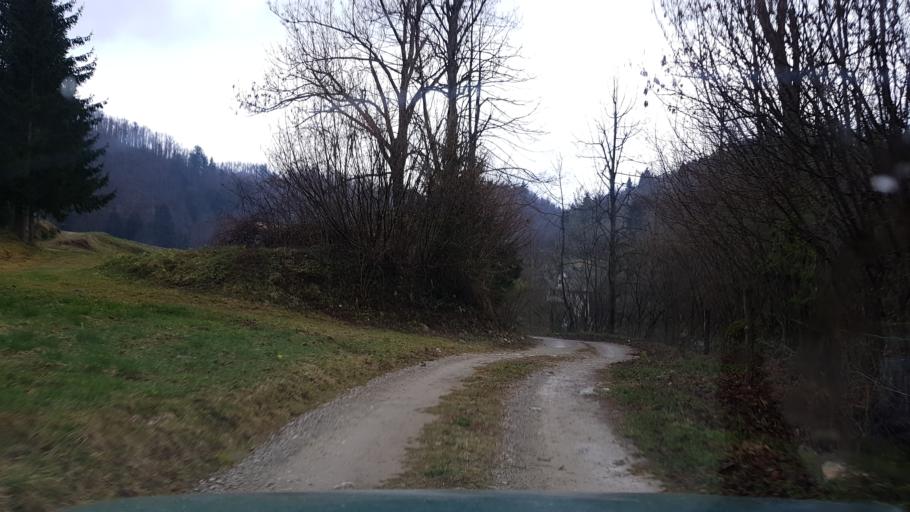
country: SI
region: Cerkno
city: Cerkno
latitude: 46.1417
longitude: 13.8842
